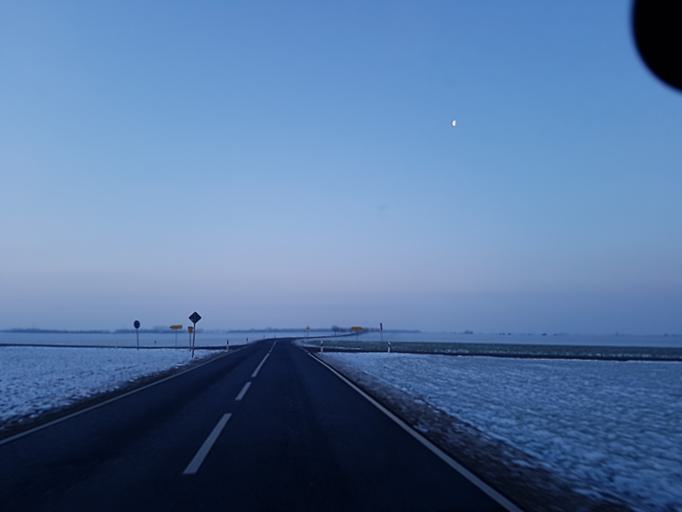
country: DE
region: Saxony
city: Strehla
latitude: 51.3291
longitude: 13.2043
